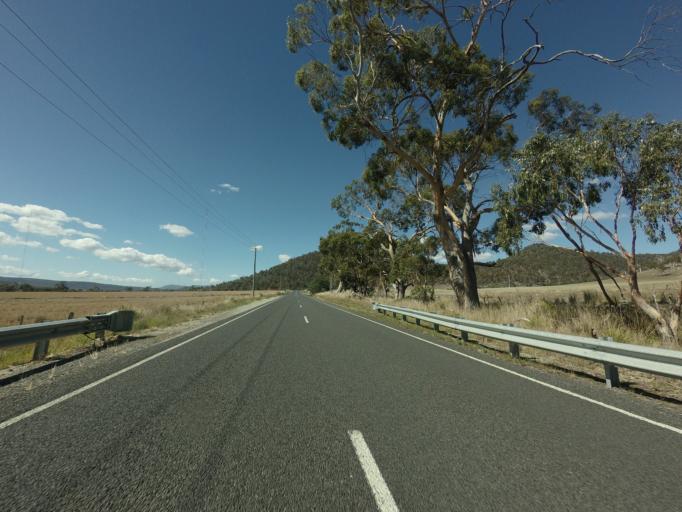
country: AU
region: Tasmania
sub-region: Break O'Day
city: St Helens
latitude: -41.6914
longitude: 147.8735
